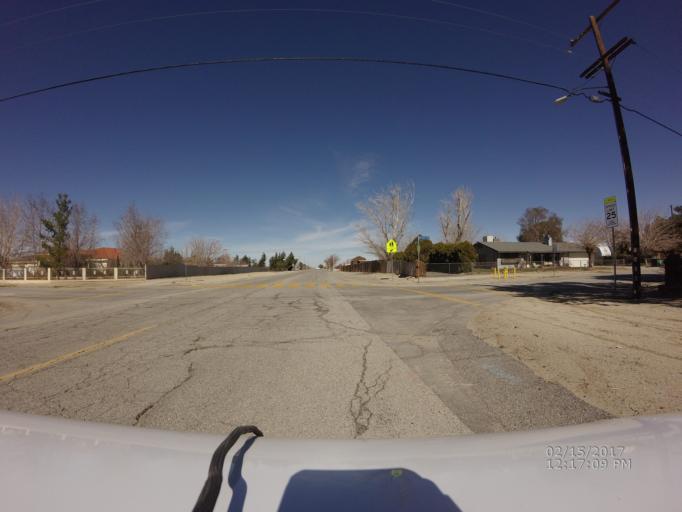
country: US
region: California
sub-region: Los Angeles County
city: Littlerock
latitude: 34.5775
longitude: -117.9612
